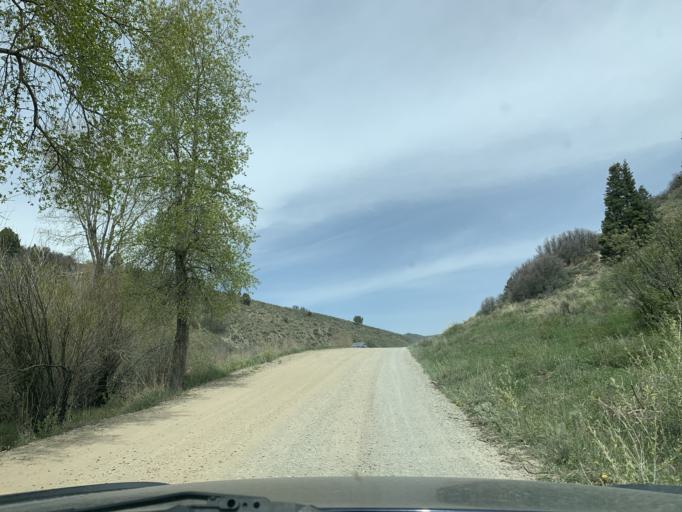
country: US
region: Utah
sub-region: Utah County
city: Mapleton
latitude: 40.1666
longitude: -111.3305
